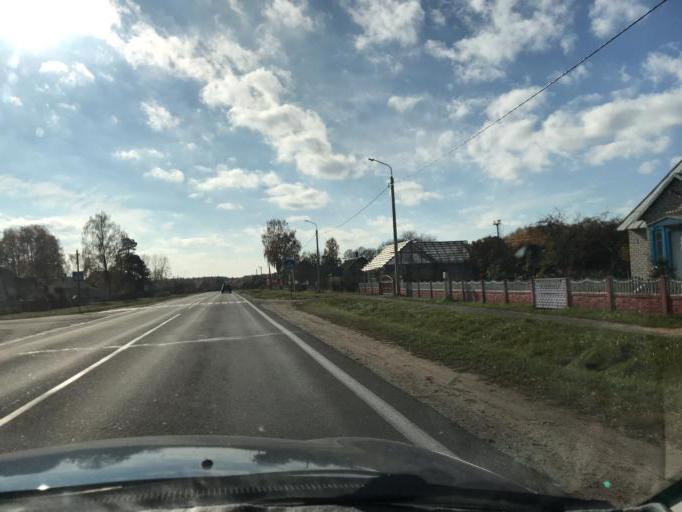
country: LT
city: Salcininkai
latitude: 54.2443
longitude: 25.3553
